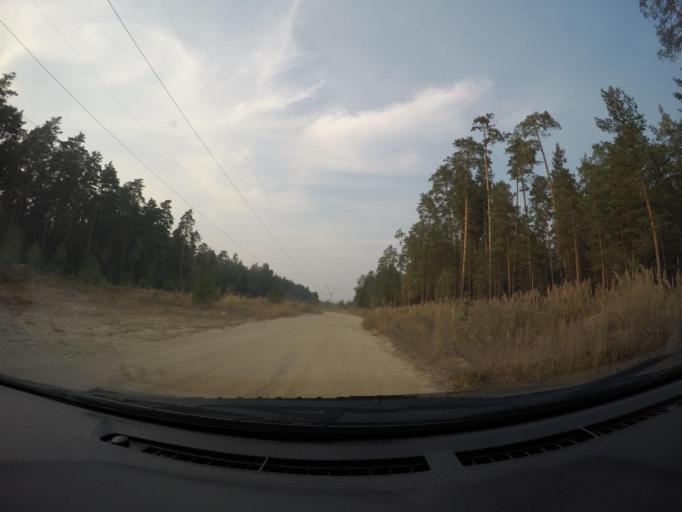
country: RU
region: Moskovskaya
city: Imeni Tsyurupy
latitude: 55.4985
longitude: 38.6881
